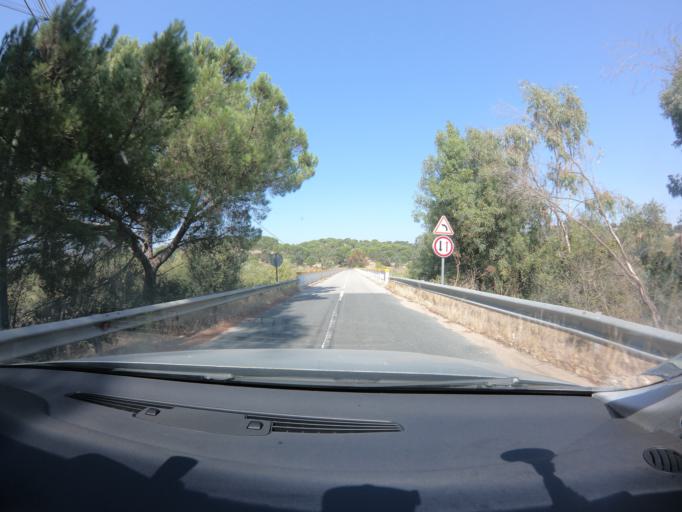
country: PT
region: Setubal
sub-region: Alcacer do Sal
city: Alcacer do Sal
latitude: 38.2705
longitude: -8.3580
